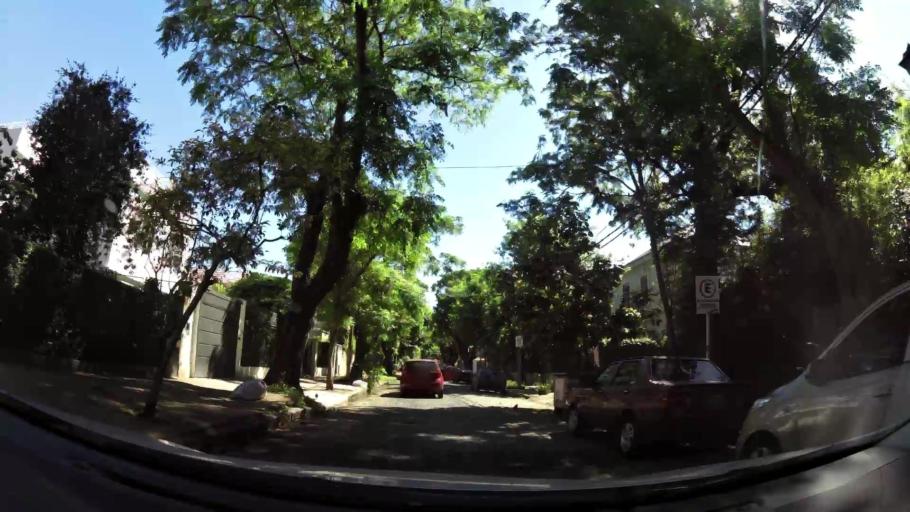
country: AR
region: Buenos Aires
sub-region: Partido de San Isidro
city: San Isidro
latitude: -34.4687
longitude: -58.5069
